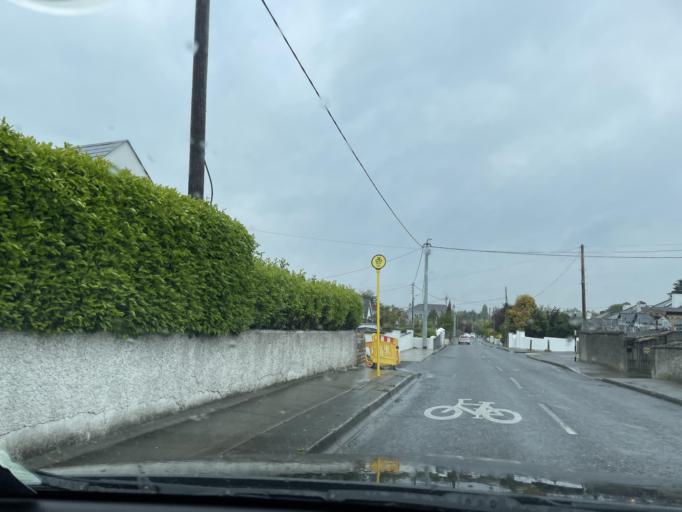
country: IE
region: Leinster
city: Dundrum
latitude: 53.2899
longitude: -6.2567
